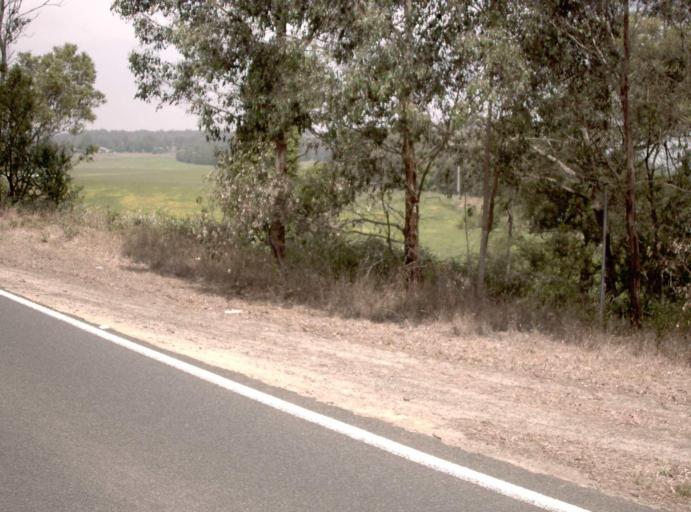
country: AU
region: Victoria
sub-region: Latrobe
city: Traralgon
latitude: -38.2964
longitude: 146.7024
